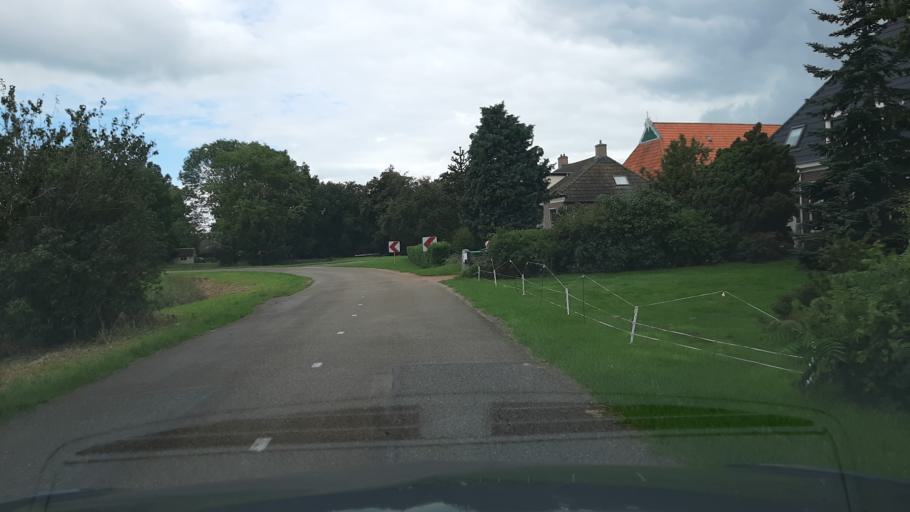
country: NL
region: Friesland
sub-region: Gemeente Weststellingwerf
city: Wolvega
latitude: 52.9136
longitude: 6.0083
